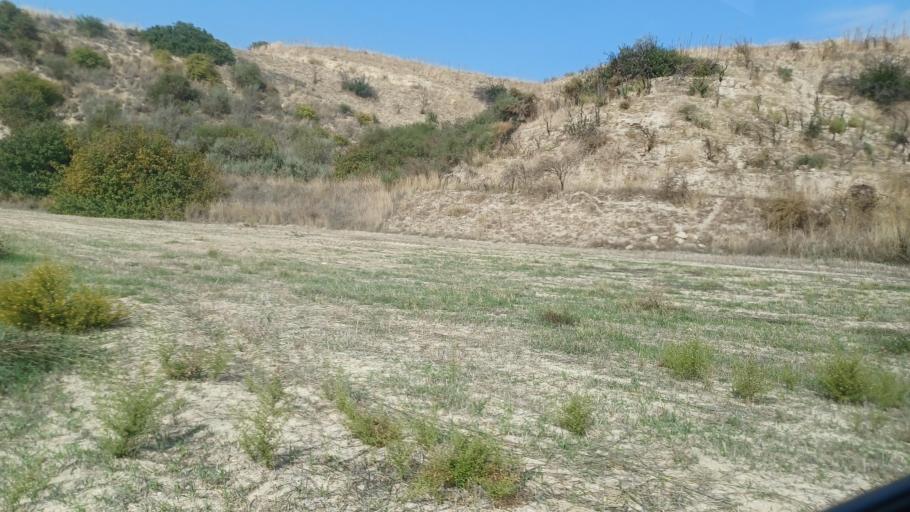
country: CY
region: Pafos
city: Polis
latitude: 34.9713
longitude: 32.4580
